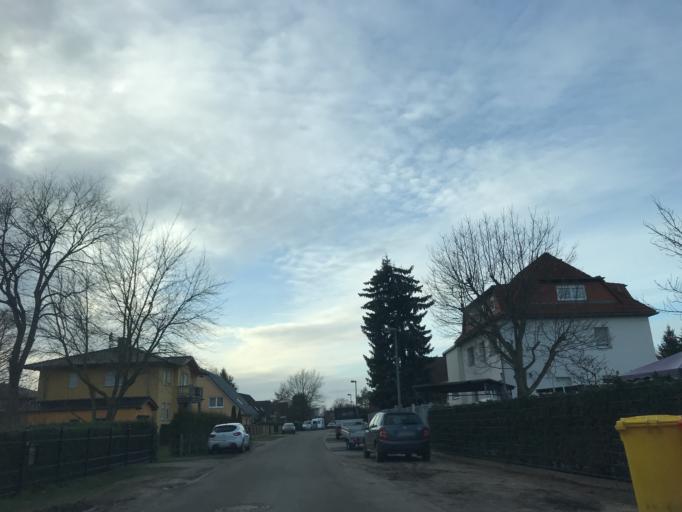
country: DE
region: Berlin
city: Staaken
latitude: 52.5510
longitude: 13.1399
